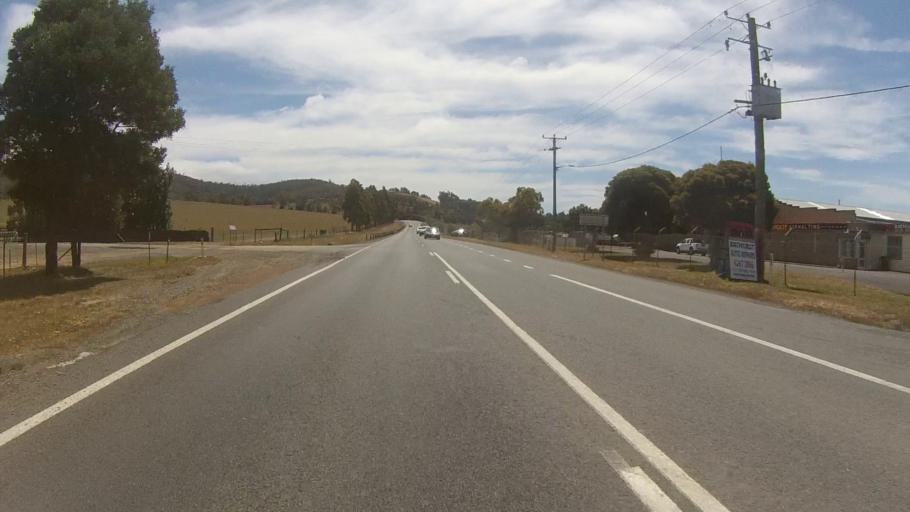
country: AU
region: Tasmania
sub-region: Kingborough
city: Margate
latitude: -43.0146
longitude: 147.2717
